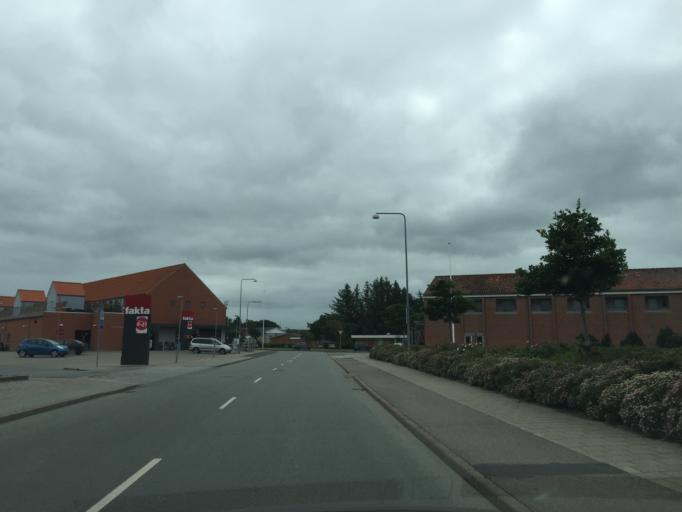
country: DK
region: South Denmark
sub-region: Tonder Kommune
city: Sherrebek
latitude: 55.1594
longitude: 8.7610
